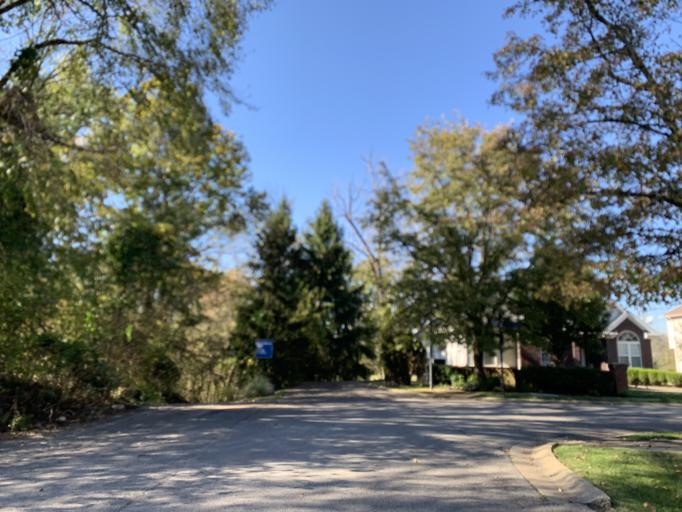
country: US
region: Indiana
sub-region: Floyd County
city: New Albany
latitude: 38.2655
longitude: -85.8270
